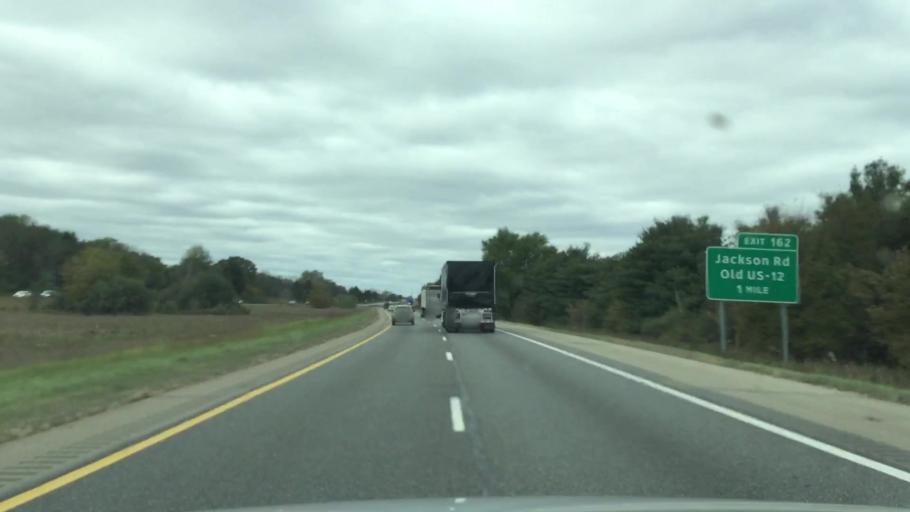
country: US
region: Michigan
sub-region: Washtenaw County
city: Chelsea
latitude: 42.2998
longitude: -83.9522
